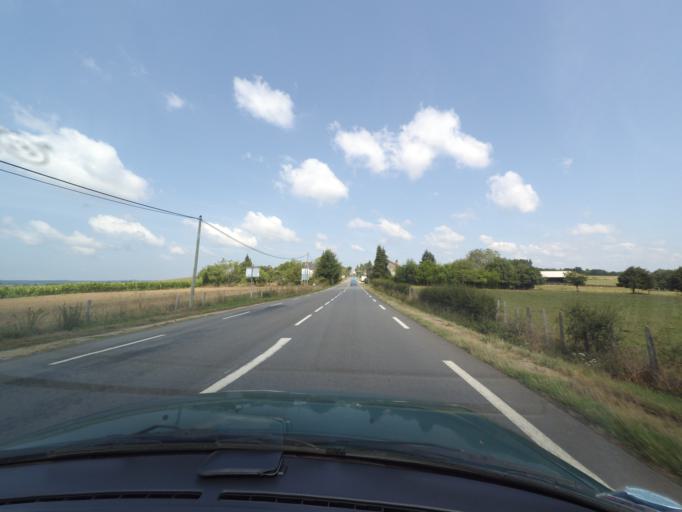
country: FR
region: Limousin
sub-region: Departement de la Haute-Vienne
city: Neuvic-Entier
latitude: 45.7330
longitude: 1.6152
